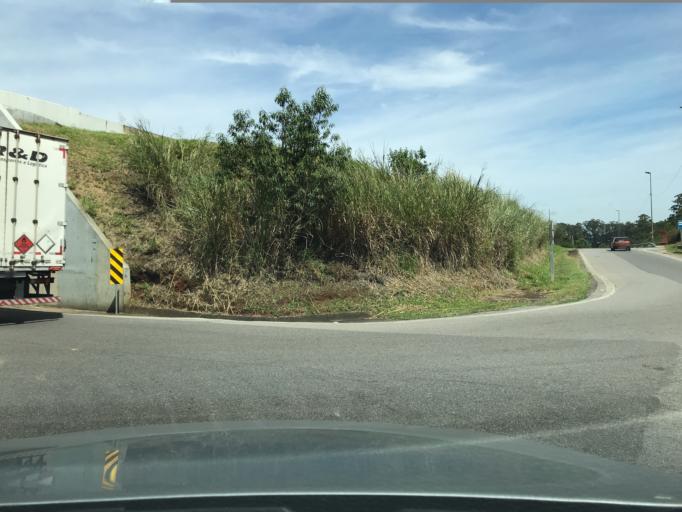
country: BR
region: Sao Paulo
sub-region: Cajamar
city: Cajamar
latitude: -23.4086
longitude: -46.8210
